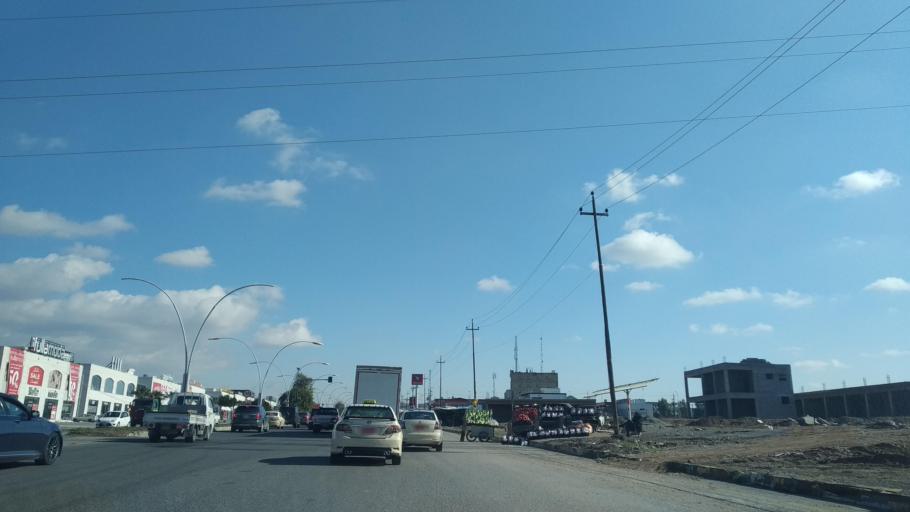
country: IQ
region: Arbil
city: Erbil
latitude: 36.1997
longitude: 44.0861
